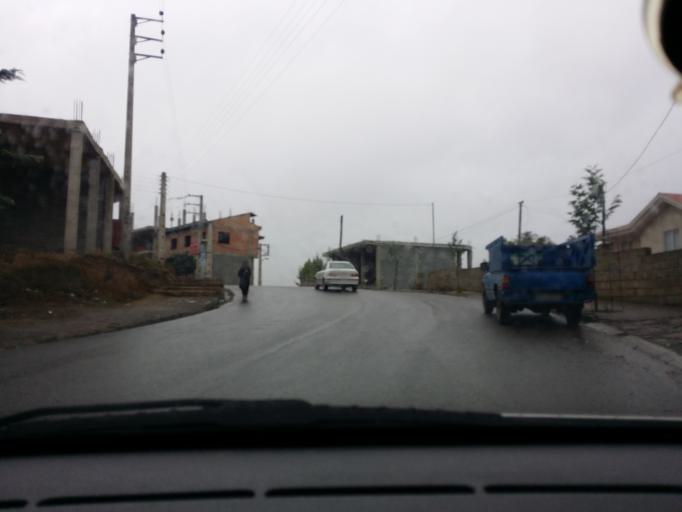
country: IR
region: Mazandaran
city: Chalus
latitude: 36.5279
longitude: 51.2308
